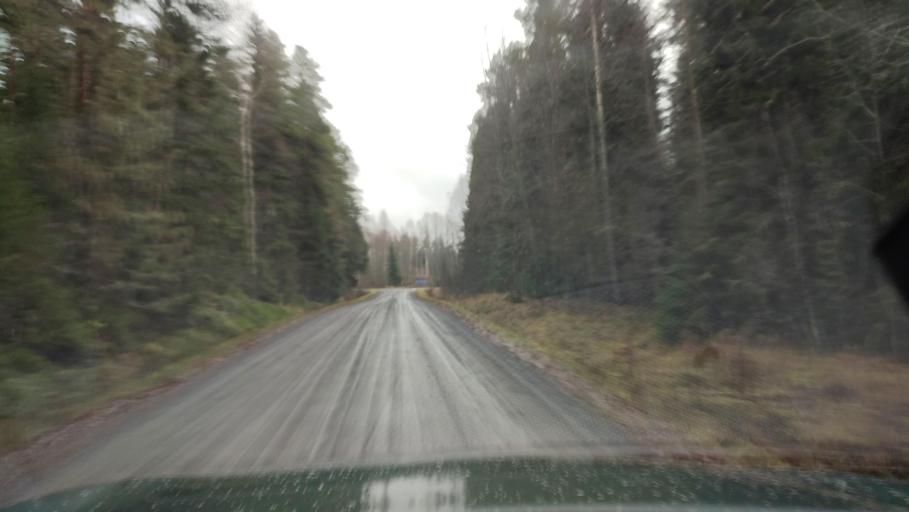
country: FI
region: Ostrobothnia
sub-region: Sydosterbotten
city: Naerpes
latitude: 62.4597
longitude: 21.4918
